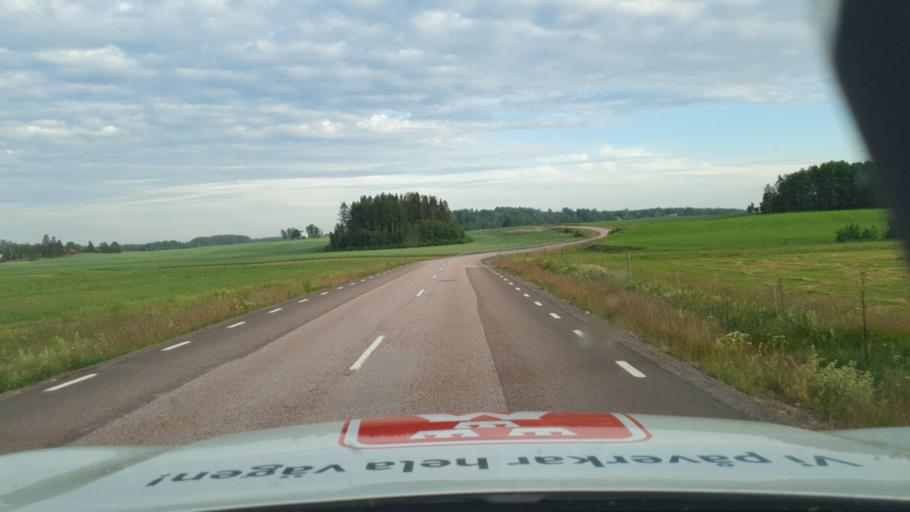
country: SE
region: Vaermland
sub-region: Karlstads Kommun
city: Molkom
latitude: 59.5685
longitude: 13.7717
